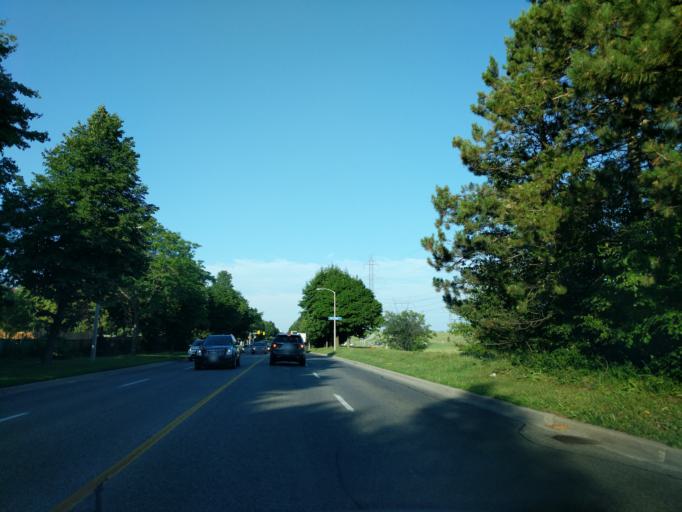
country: CA
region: Ontario
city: Scarborough
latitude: 43.8175
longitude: -79.2742
